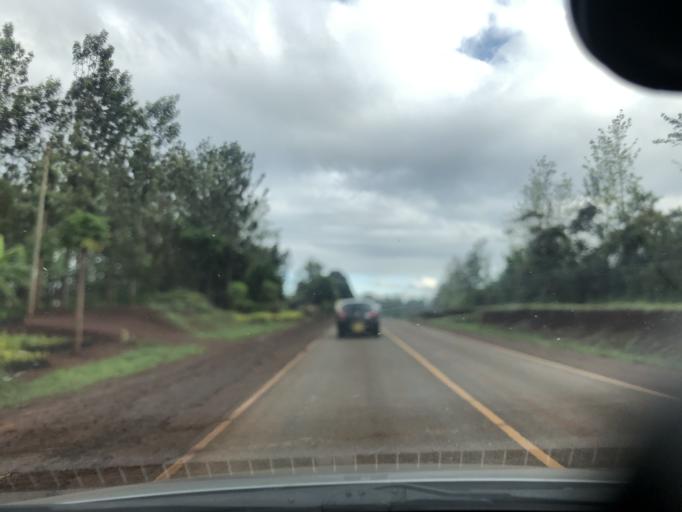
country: KE
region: Murang'a District
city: Maragua
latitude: -0.8337
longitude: 37.1375
